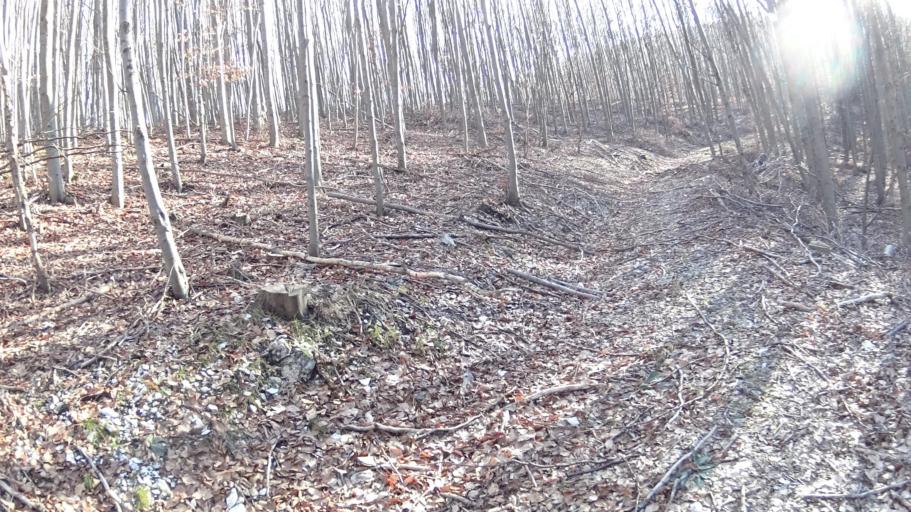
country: HU
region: Heves
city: Szilvasvarad
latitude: 48.0827
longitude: 20.4644
